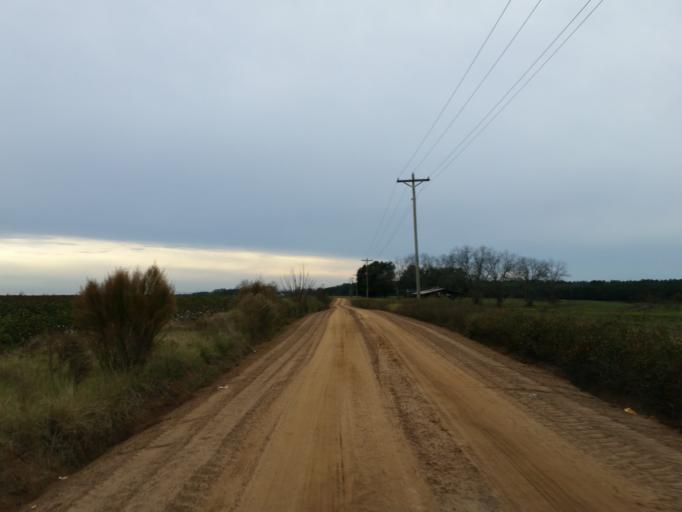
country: US
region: Georgia
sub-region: Crisp County
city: Cordele
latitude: 31.8988
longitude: -83.7144
